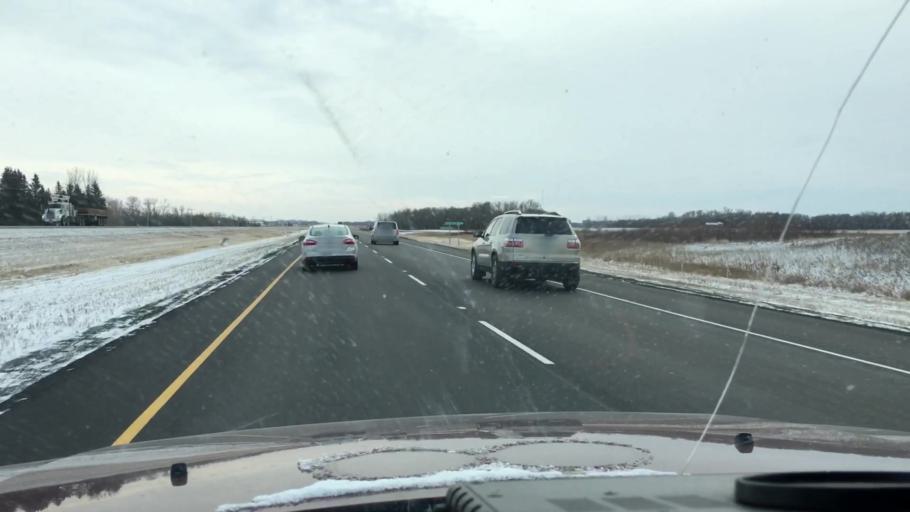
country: CA
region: Saskatchewan
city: Saskatoon
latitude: 52.0154
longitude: -106.5752
